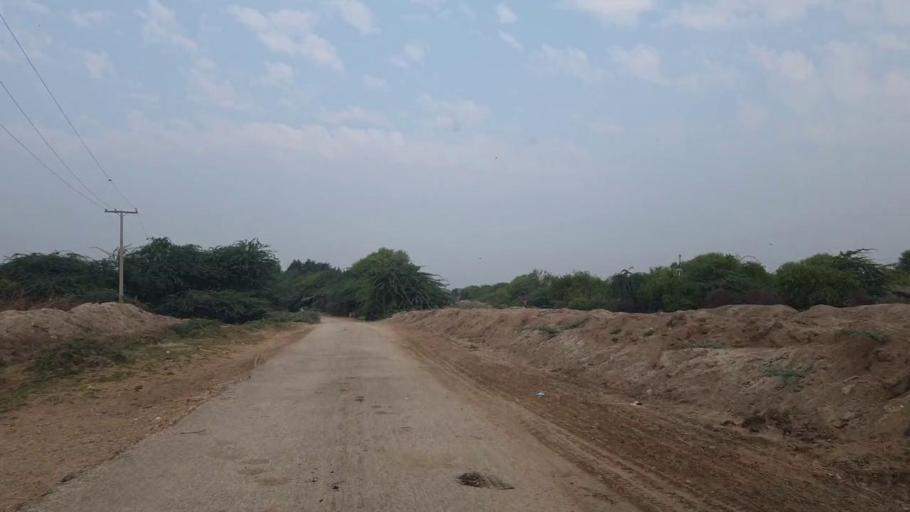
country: PK
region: Sindh
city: Talhar
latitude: 24.8395
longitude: 68.8780
